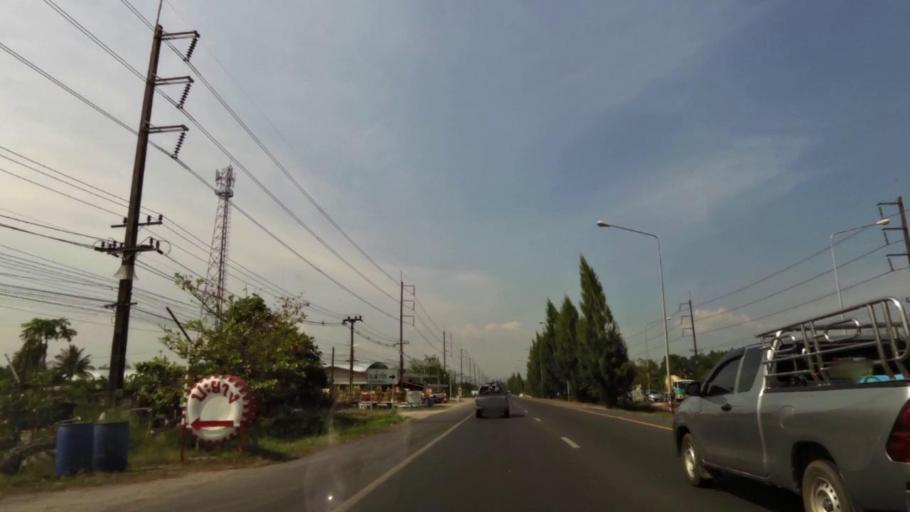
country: TH
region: Chanthaburi
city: Chanthaburi
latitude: 12.6382
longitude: 102.1358
